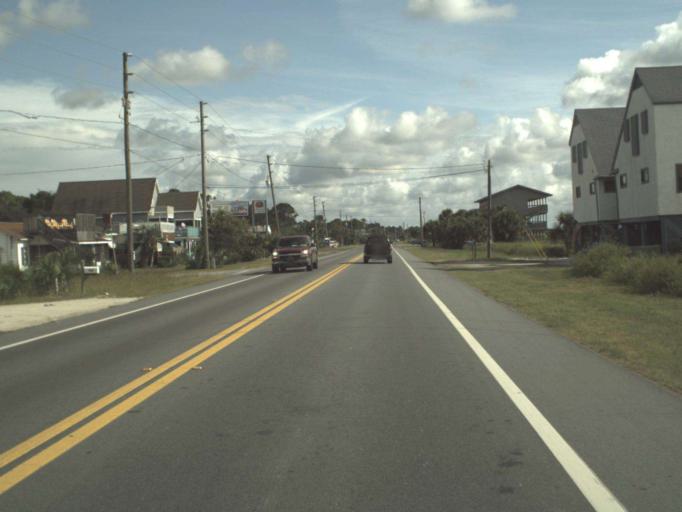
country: US
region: Florida
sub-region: Bay County
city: Mexico Beach
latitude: 29.9008
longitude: -85.3647
